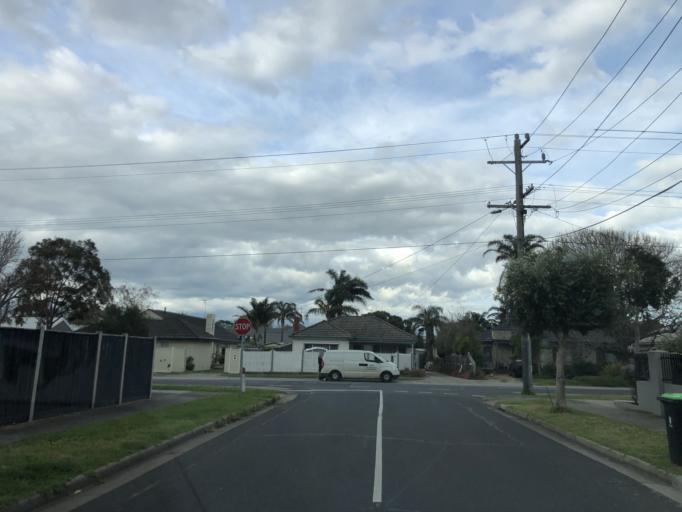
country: AU
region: Victoria
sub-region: Kingston
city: Bonbeach
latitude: -38.0602
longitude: 145.1253
